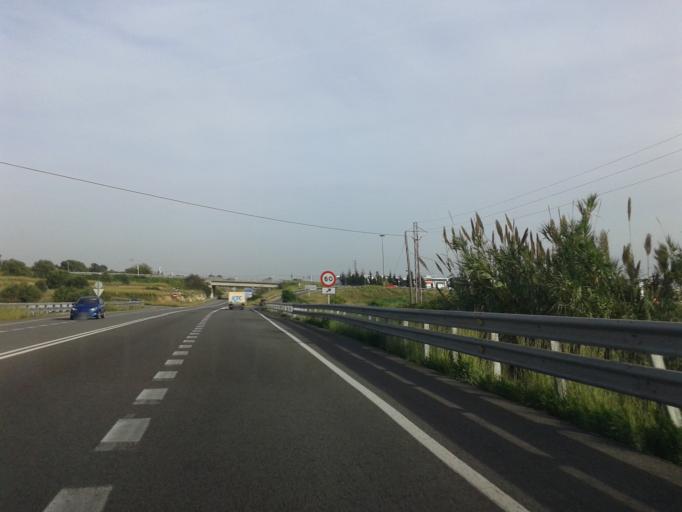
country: ES
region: Catalonia
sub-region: Provincia de Barcelona
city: Vilanova i la Geltru
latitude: 41.2368
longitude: 1.7307
